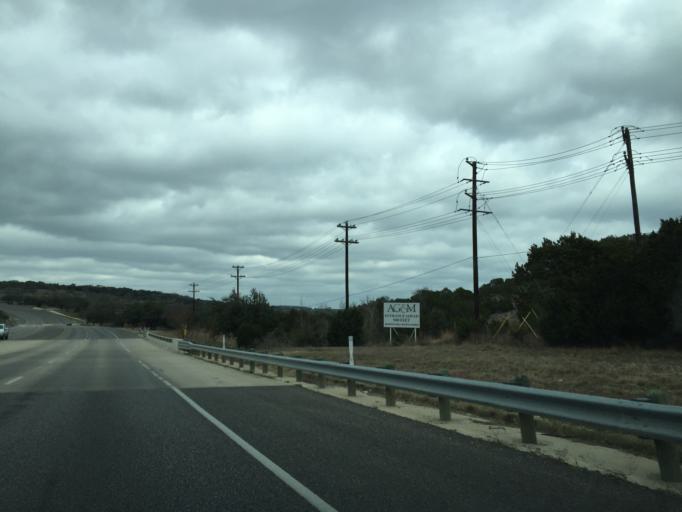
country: US
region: Texas
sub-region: Travis County
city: The Hills
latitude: 30.3372
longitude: -98.0330
